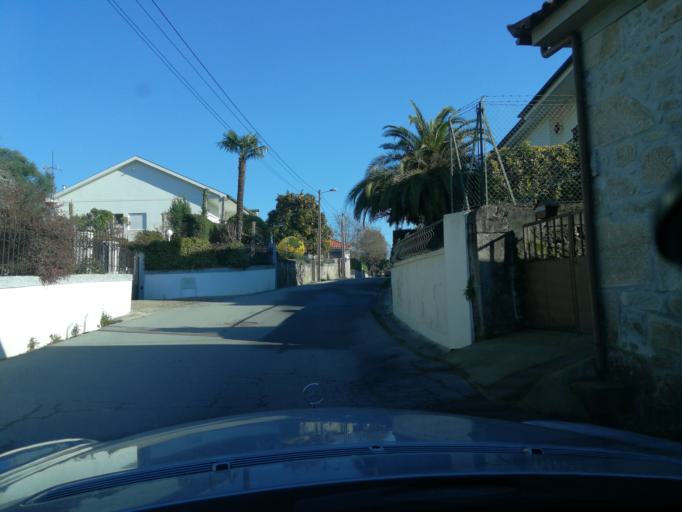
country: PT
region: Braga
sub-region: Braga
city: Adaufe
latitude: 41.6151
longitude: -8.4071
